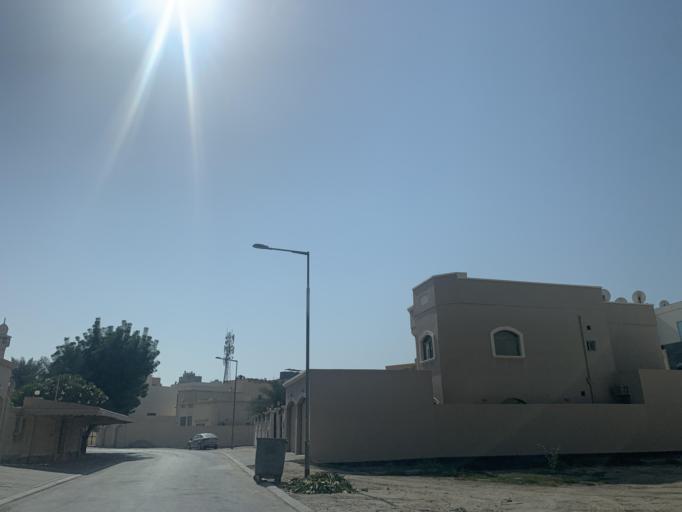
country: BH
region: Central Governorate
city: Madinat Hamad
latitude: 26.1367
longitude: 50.4939
